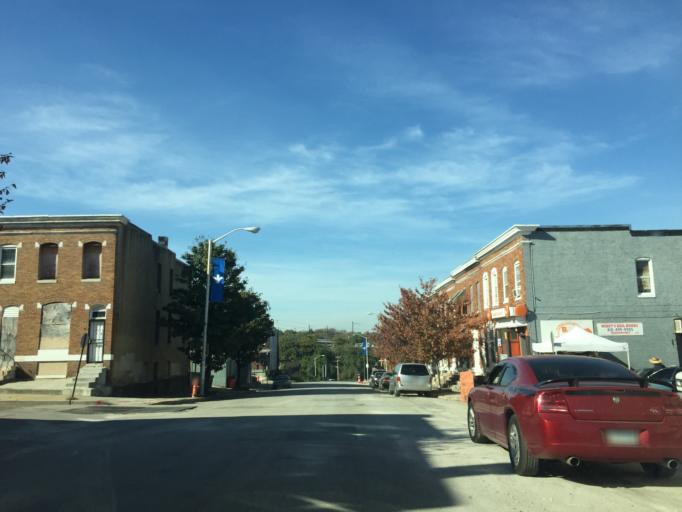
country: US
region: Maryland
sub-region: City of Baltimore
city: Baltimore
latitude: 39.2890
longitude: -76.6534
